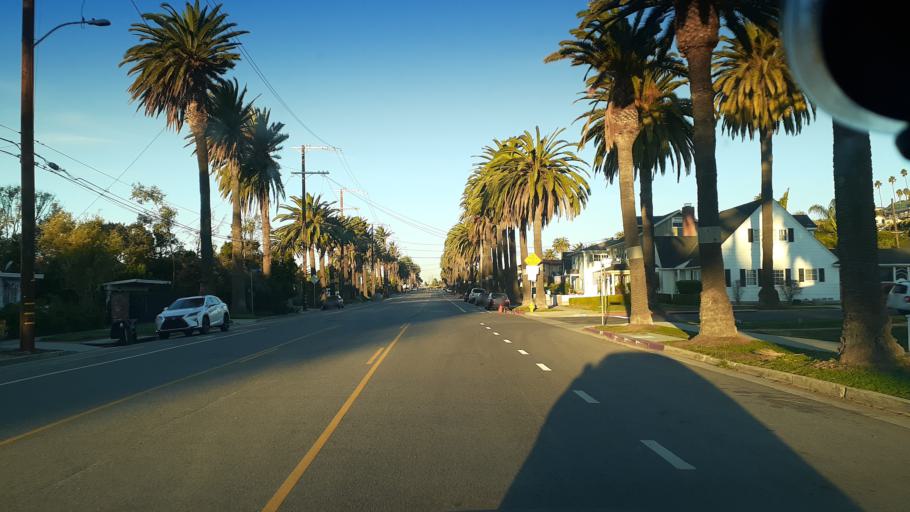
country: US
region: California
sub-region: Los Angeles County
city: San Pedro
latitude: 33.7131
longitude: -118.3056
